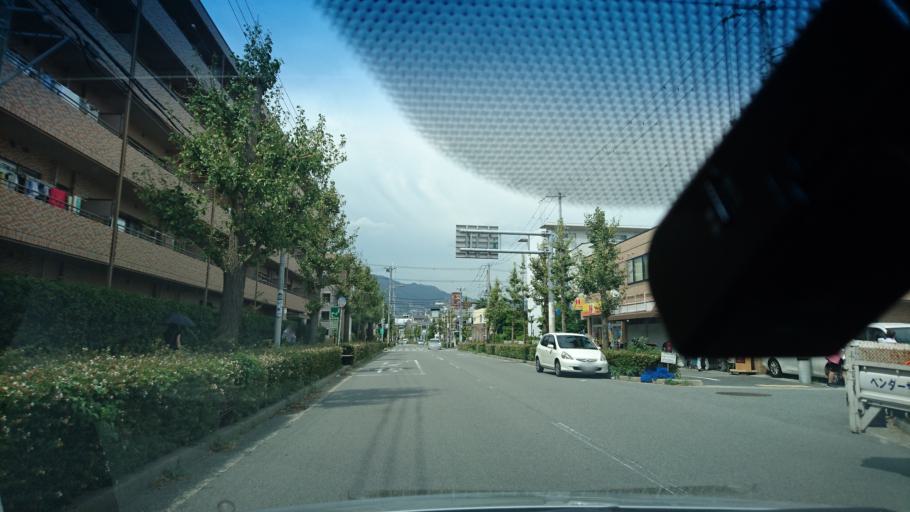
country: JP
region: Hyogo
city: Ashiya
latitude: 34.7264
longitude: 135.3190
